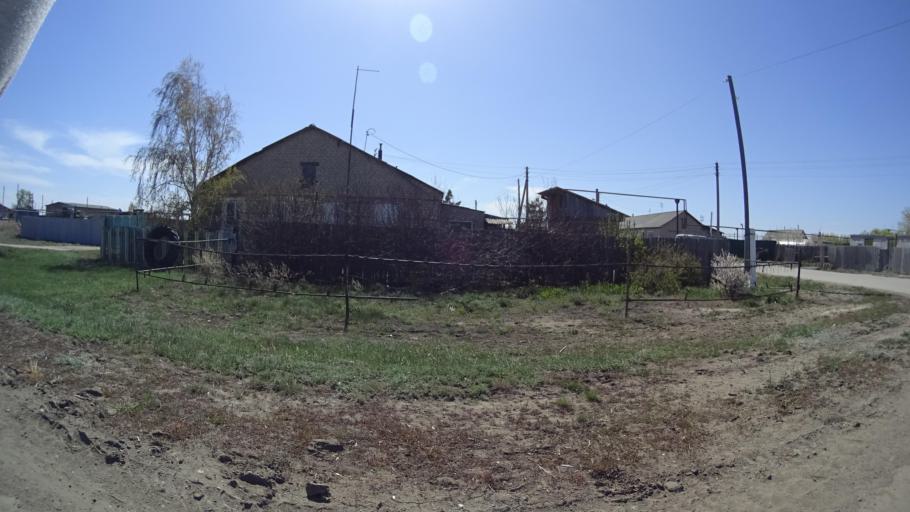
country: RU
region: Chelyabinsk
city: Chesma
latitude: 53.7905
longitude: 61.0407
